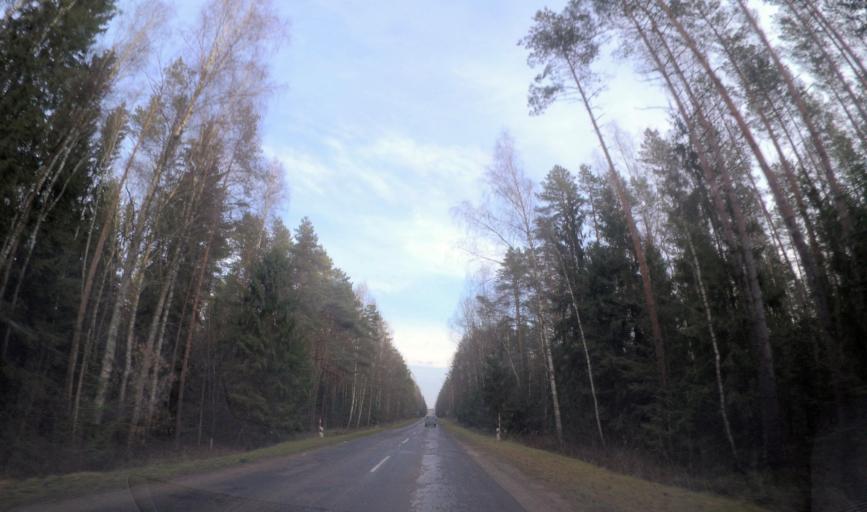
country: LT
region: Alytaus apskritis
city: Druskininkai
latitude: 53.8191
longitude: 24.0473
